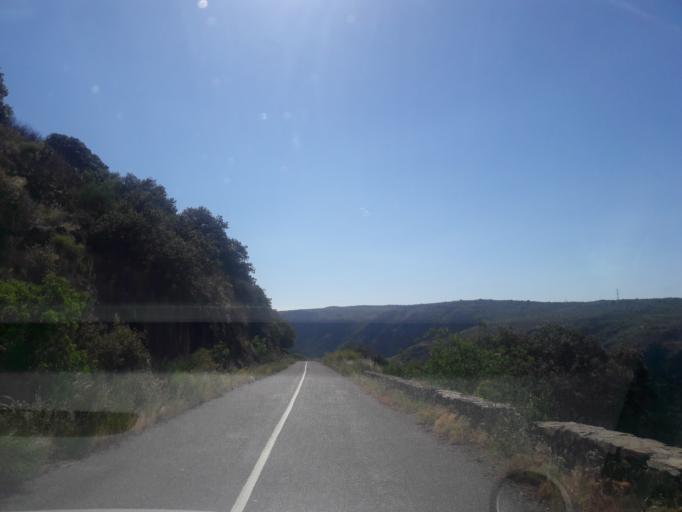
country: ES
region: Castille and Leon
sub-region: Provincia de Salamanca
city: Saucelle
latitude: 41.0330
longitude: -6.7531
